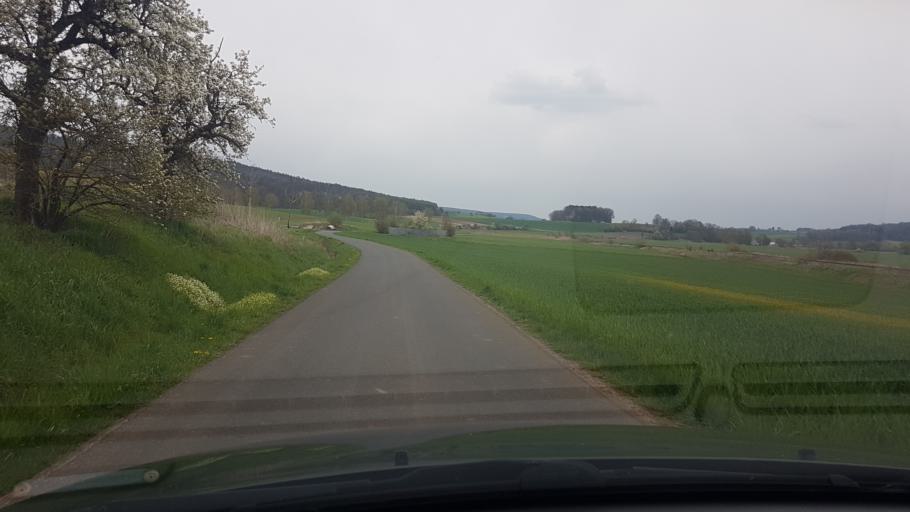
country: DE
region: Bavaria
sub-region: Regierungsbezirk Unterfranken
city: Rentweinsdorf
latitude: 50.0603
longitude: 10.8150
